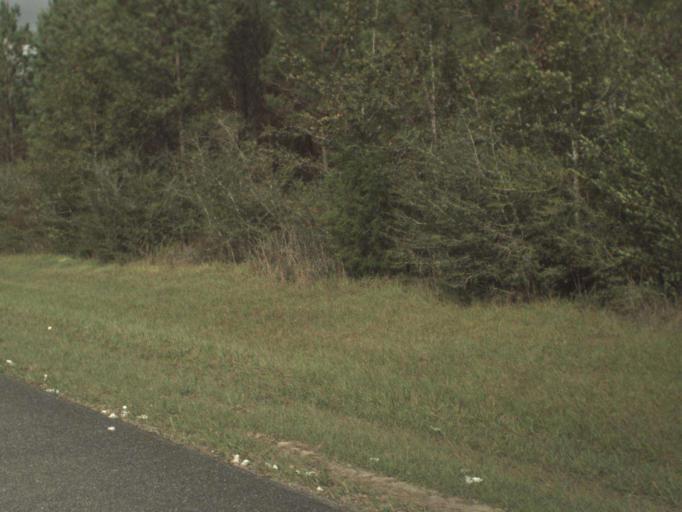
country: US
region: Florida
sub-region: Santa Rosa County
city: Point Baker
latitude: 30.8080
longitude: -87.1265
